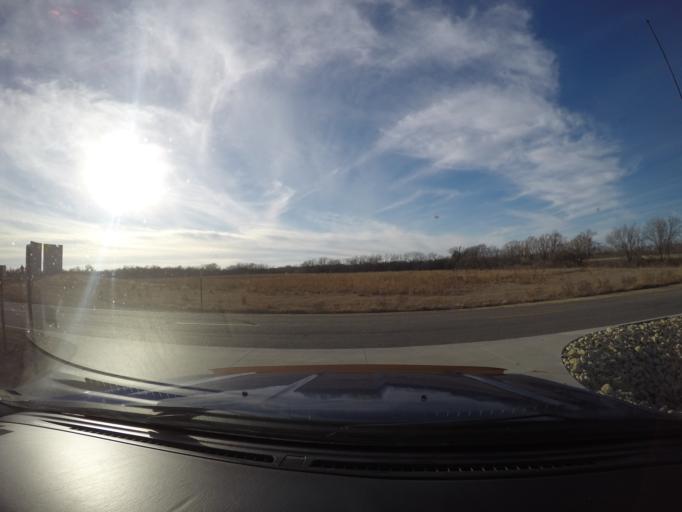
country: US
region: Kansas
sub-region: Harvey County
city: North Newton
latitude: 38.0627
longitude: -97.3366
